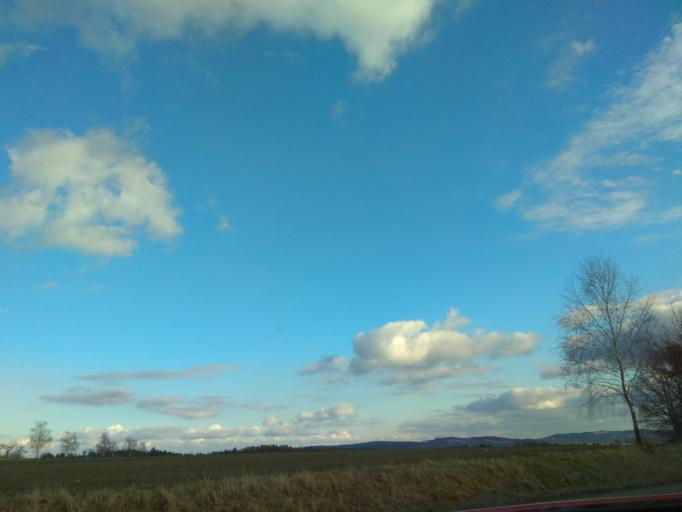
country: CZ
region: Jihocesky
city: Hrdejovice
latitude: 49.0331
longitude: 14.4825
